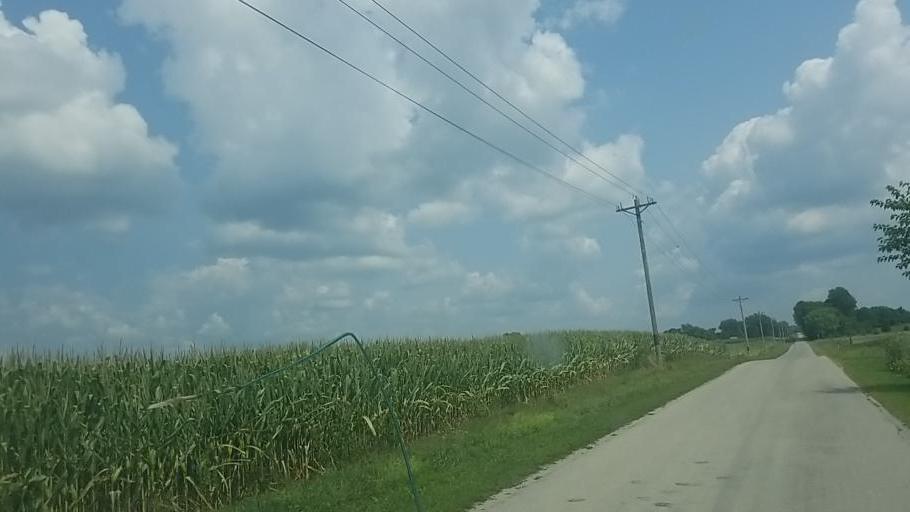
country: US
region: Ohio
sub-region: Wyandot County
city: Upper Sandusky
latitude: 40.9209
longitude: -83.1543
